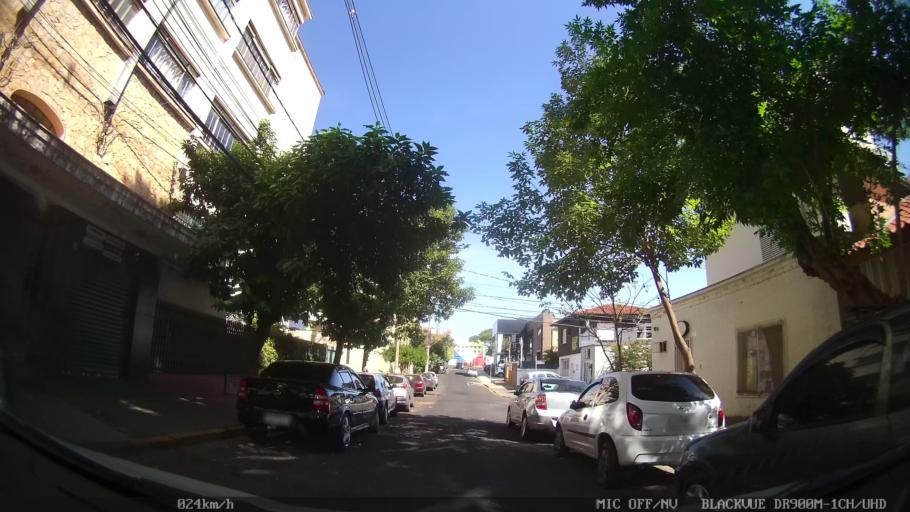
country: BR
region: Sao Paulo
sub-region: Ribeirao Preto
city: Ribeirao Preto
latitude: -21.1808
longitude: -47.8152
